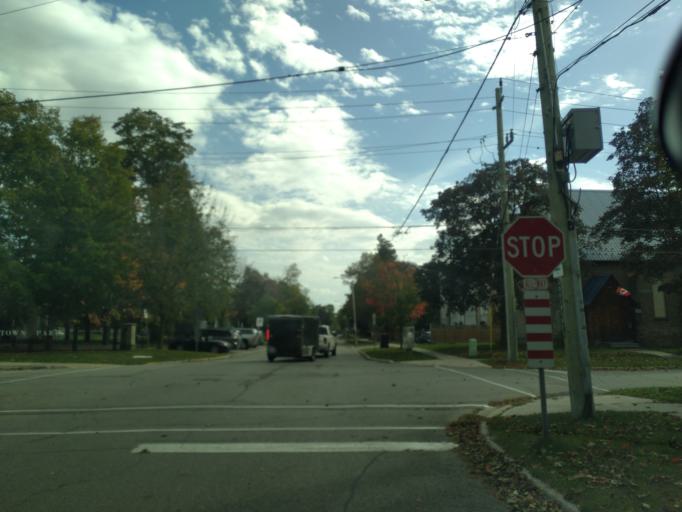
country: CA
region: Ontario
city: Newmarket
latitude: 43.9990
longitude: -79.4636
